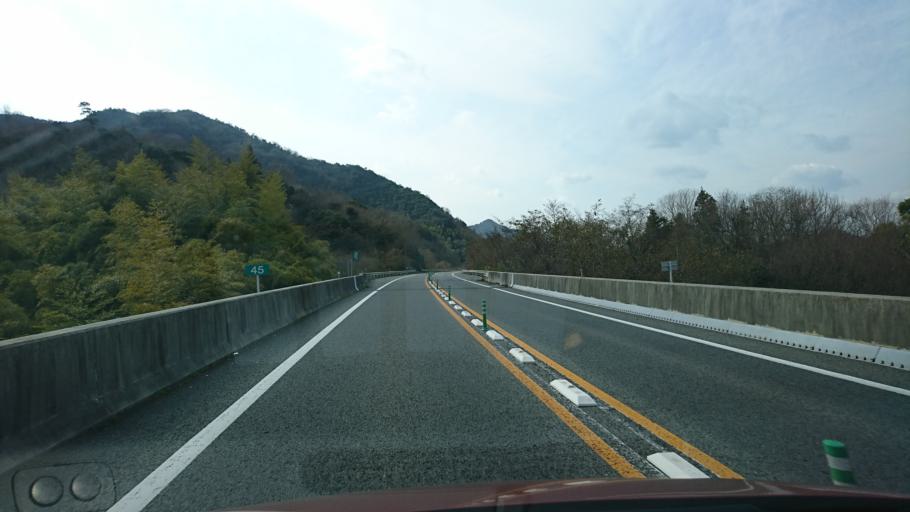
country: JP
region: Hiroshima
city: Innoshima
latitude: 34.1352
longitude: 133.0514
